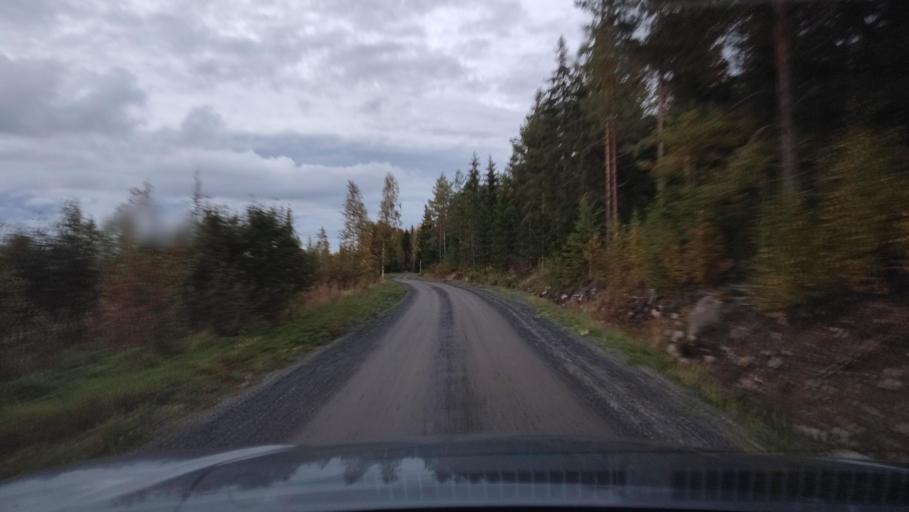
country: FI
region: Ostrobothnia
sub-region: Sydosterbotten
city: Kristinestad
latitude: 62.2785
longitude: 21.5151
